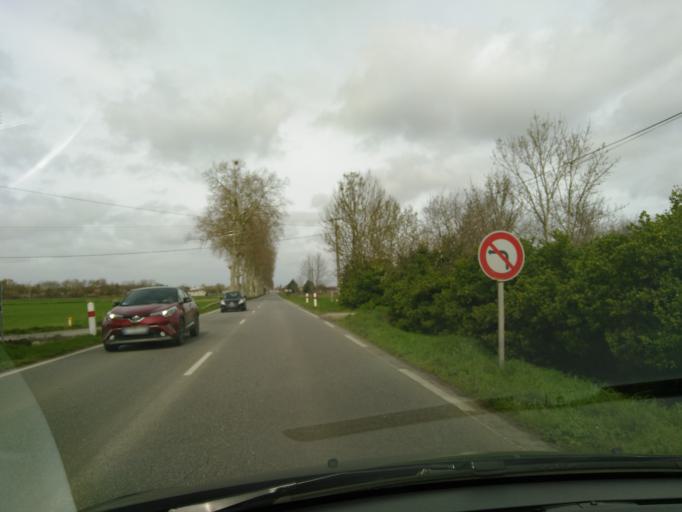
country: FR
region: Midi-Pyrenees
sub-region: Departement de la Haute-Garonne
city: Merville
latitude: 43.7491
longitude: 1.3058
